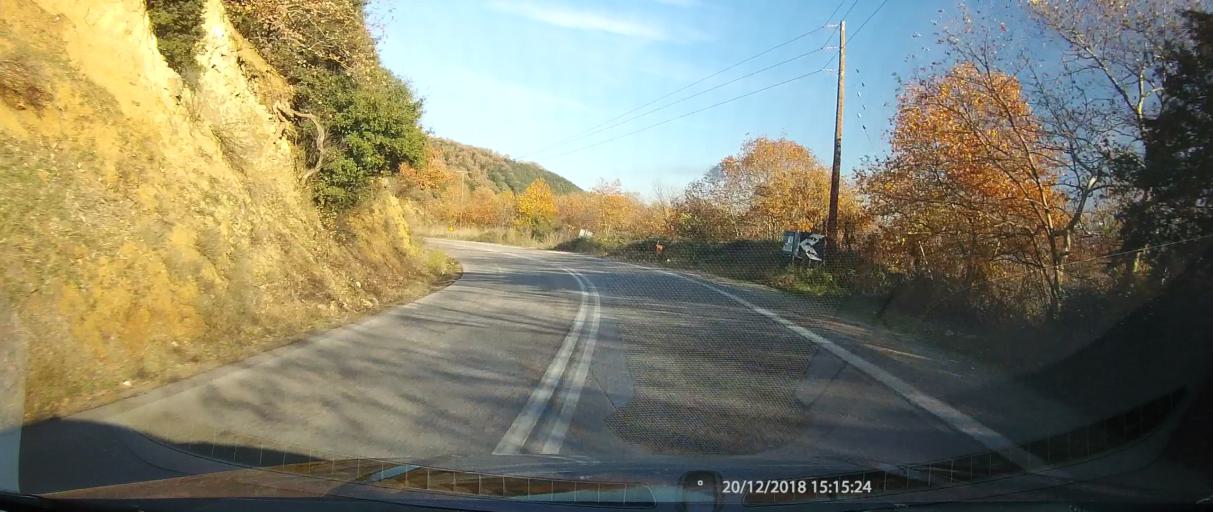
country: GR
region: Central Greece
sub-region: Nomos Fthiotidos
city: Makrakomi
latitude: 38.9291
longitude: 21.9919
